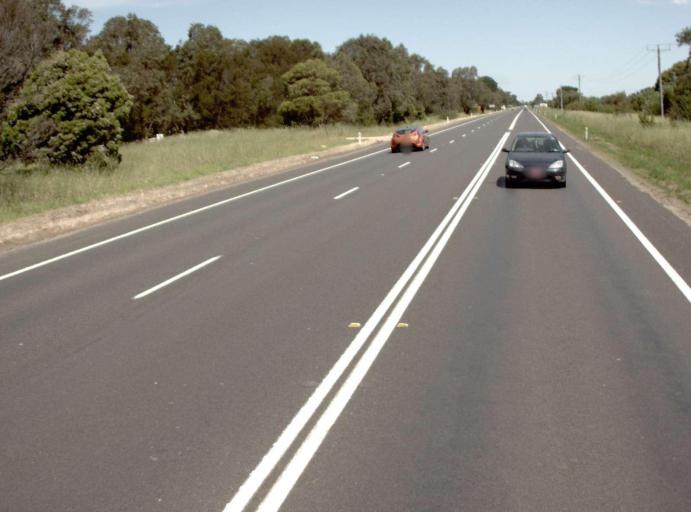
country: AU
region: Victoria
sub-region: Wellington
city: Sale
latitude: -38.0400
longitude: 147.0611
